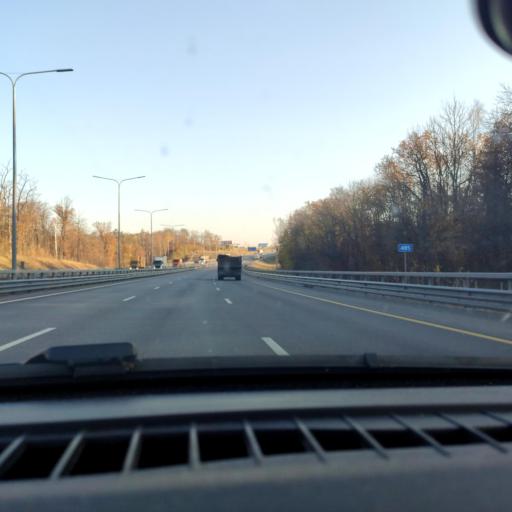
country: RU
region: Voronezj
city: Ramon'
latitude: 51.8304
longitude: 39.2423
